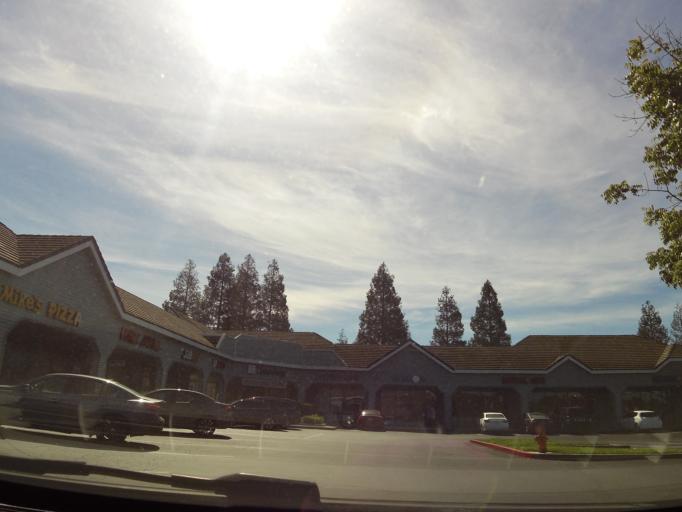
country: US
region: California
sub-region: Alameda County
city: Pleasanton
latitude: 37.6511
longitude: -121.8789
